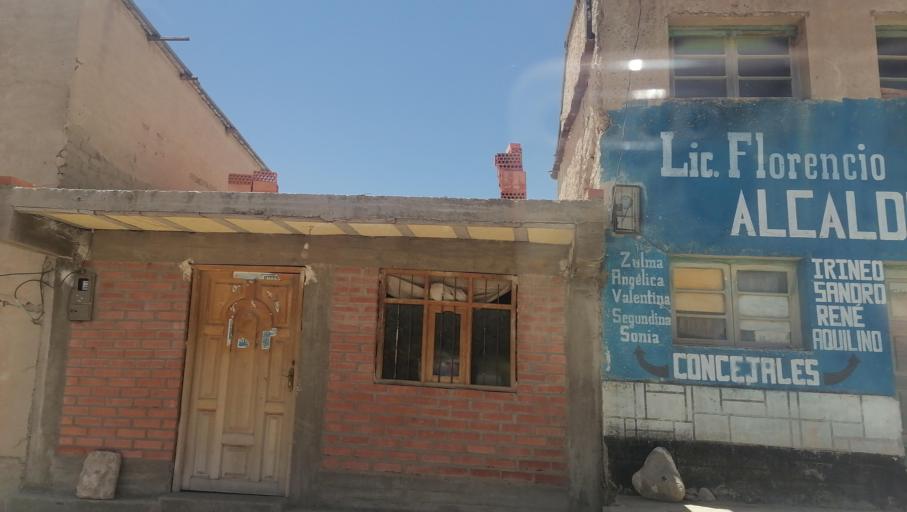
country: BO
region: Oruro
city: Challapata
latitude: -19.1961
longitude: -67.0614
